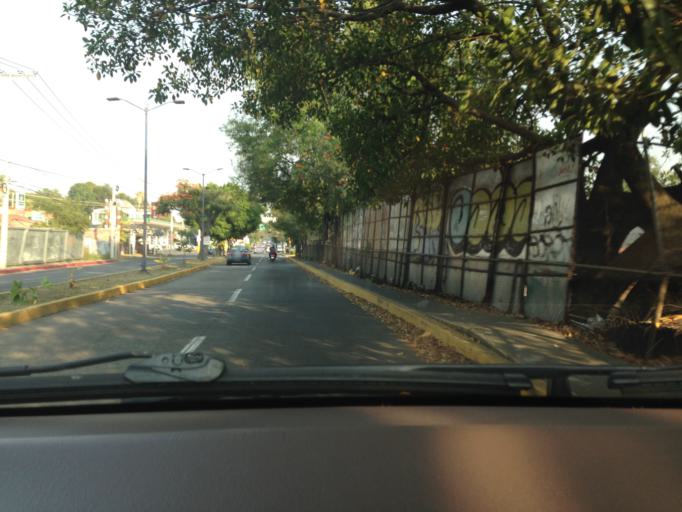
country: MX
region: Morelos
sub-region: Cuernavaca
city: Fraccionamiento Lomas de Ahuatlan
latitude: 18.9570
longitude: -99.2391
